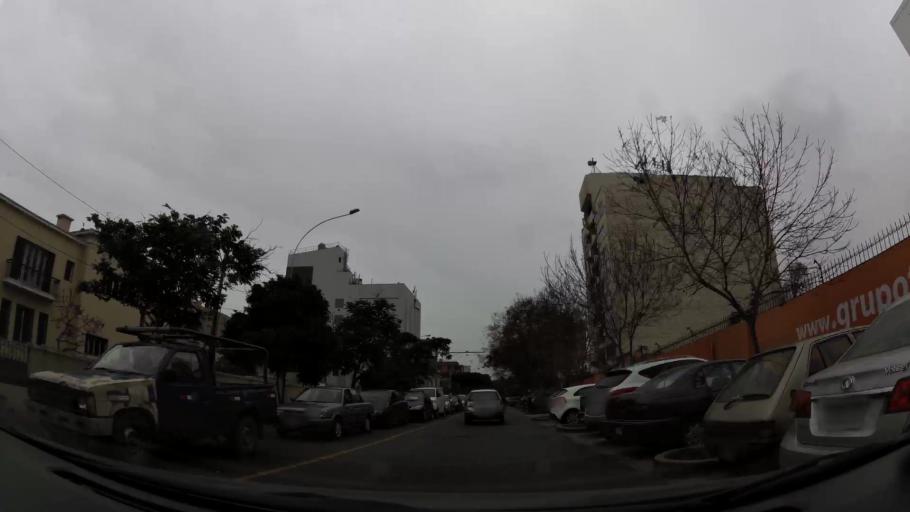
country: PE
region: Lima
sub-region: Lima
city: San Isidro
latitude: -12.0927
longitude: -77.0386
